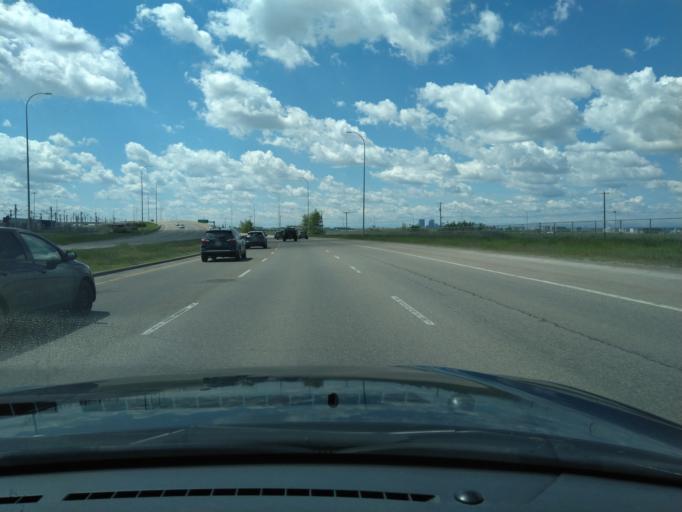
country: CA
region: Alberta
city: Calgary
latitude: 51.1064
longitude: -113.9801
